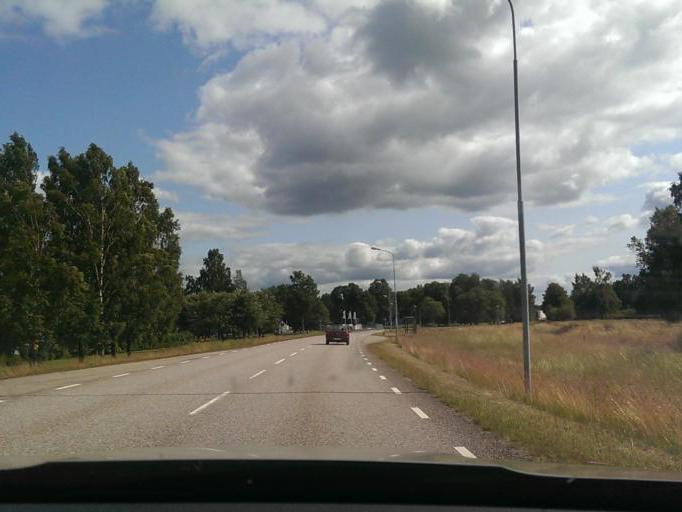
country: SE
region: Kronoberg
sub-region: Ljungby Kommun
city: Lagan
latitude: 56.9204
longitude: 13.9897
